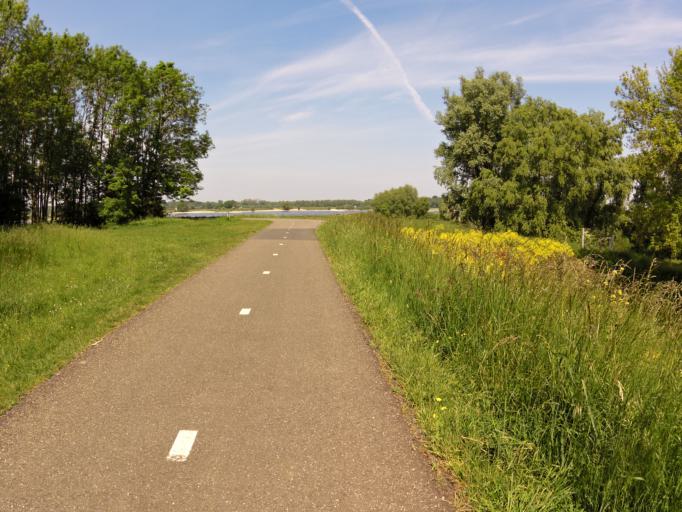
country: NL
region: Gelderland
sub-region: Gemeente Neerijnen
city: Neerijnen
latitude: 51.8165
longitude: 5.2827
